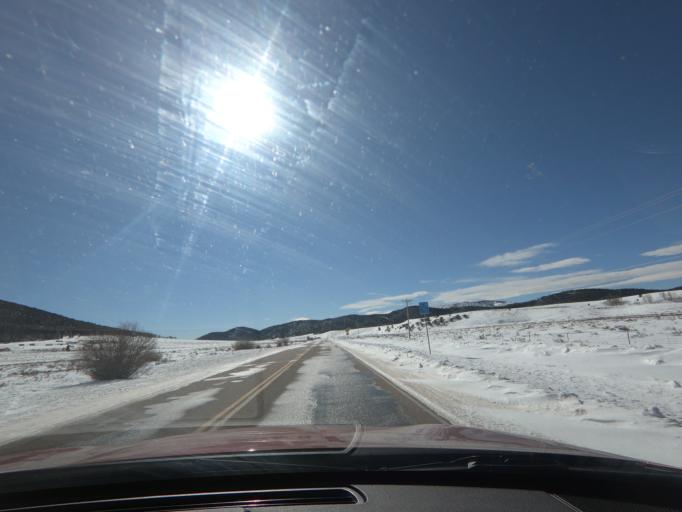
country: US
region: Colorado
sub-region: Teller County
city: Cripple Creek
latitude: 38.7797
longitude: -105.1220
